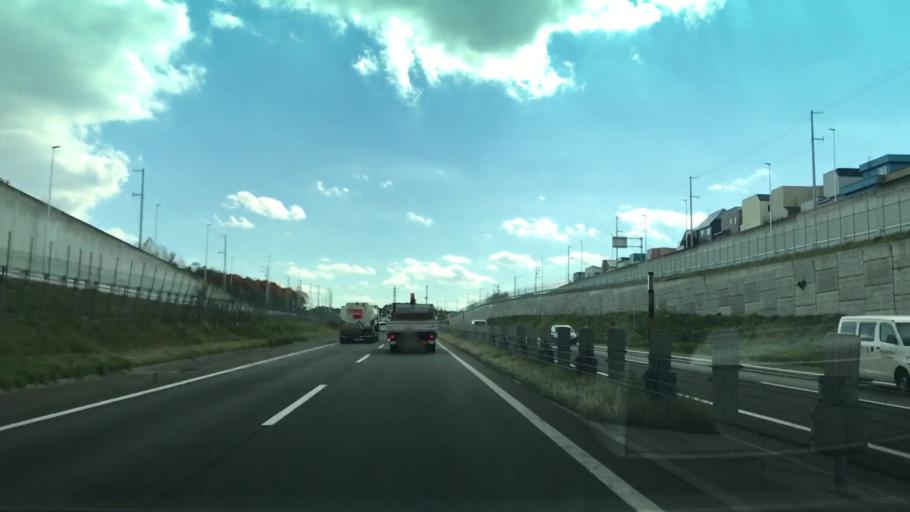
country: JP
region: Hokkaido
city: Kitahiroshima
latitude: 42.9926
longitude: 141.4693
